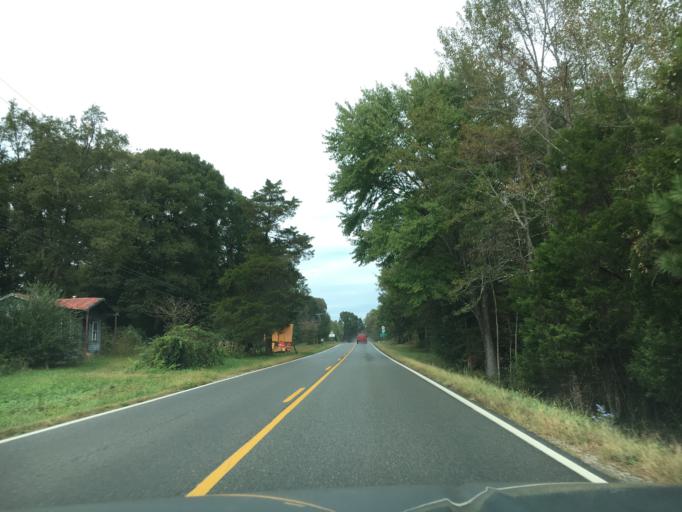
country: US
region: Virginia
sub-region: Goochland County
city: Goochland
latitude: 37.7305
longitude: -77.8360
